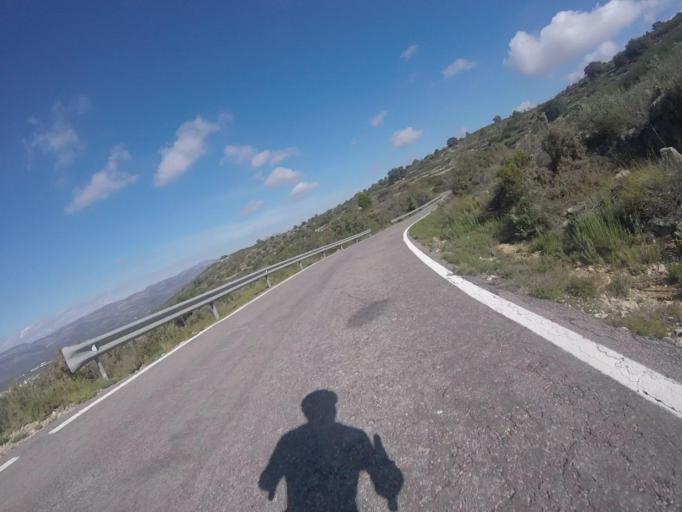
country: ES
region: Valencia
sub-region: Provincia de Castello
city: Albocasser
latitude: 40.3516
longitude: 0.0465
